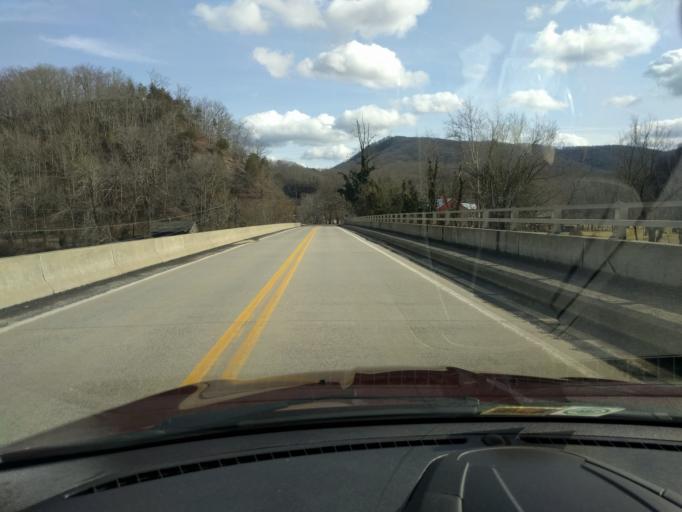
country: US
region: West Virginia
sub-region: Greenbrier County
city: Lewisburg
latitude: 37.7823
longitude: -80.3978
